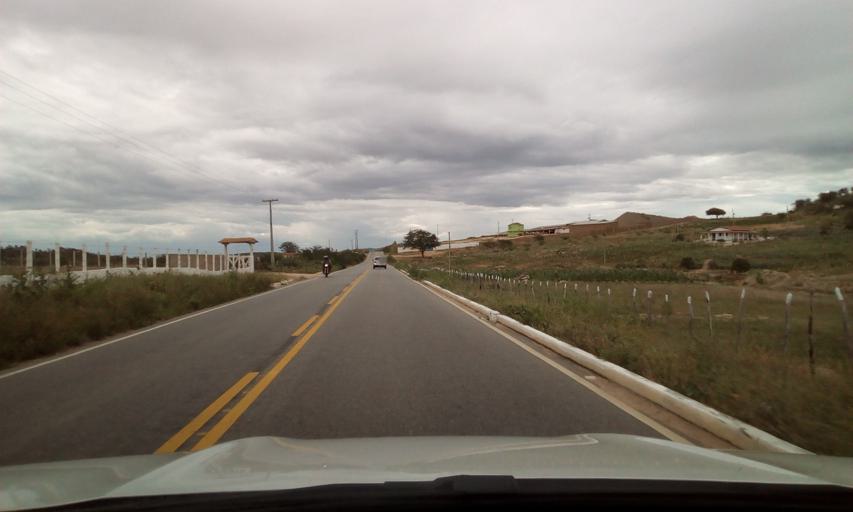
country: BR
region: Paraiba
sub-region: Picui
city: Picui
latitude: -6.5481
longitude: -36.2979
